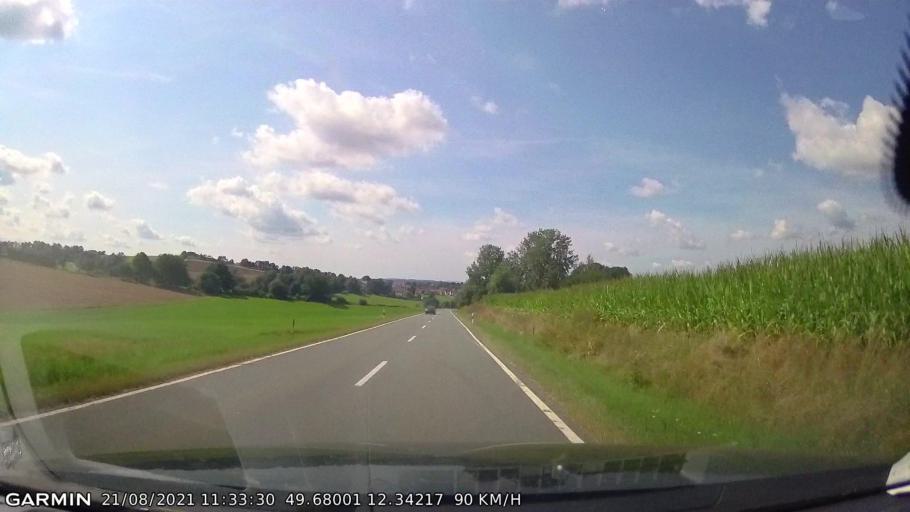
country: DE
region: Bavaria
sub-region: Upper Palatinate
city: Waldthurn
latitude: 49.6799
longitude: 12.3421
